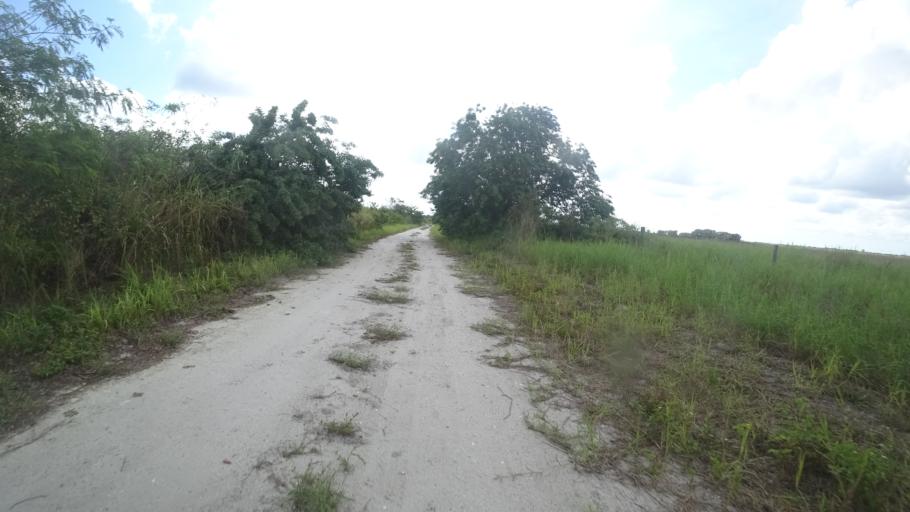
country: US
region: Florida
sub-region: Hillsborough County
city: Wimauma
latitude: 27.5786
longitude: -82.2676
